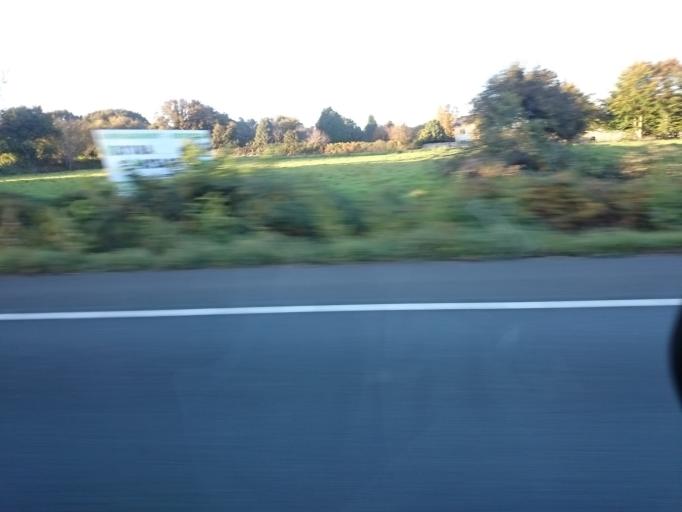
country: FR
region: Brittany
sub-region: Departement des Cotes-d'Armor
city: Belle-Isle-en-Terre
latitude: 48.5489
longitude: -3.4136
